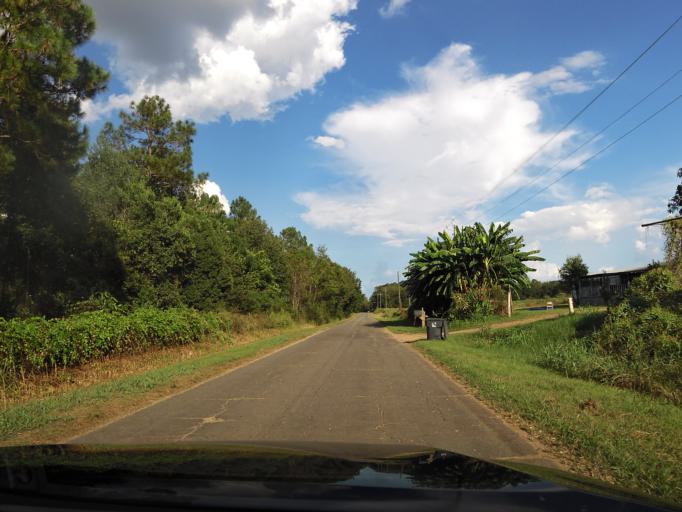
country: US
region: Georgia
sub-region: Brooks County
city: Quitman
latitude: 30.7773
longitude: -83.6077
